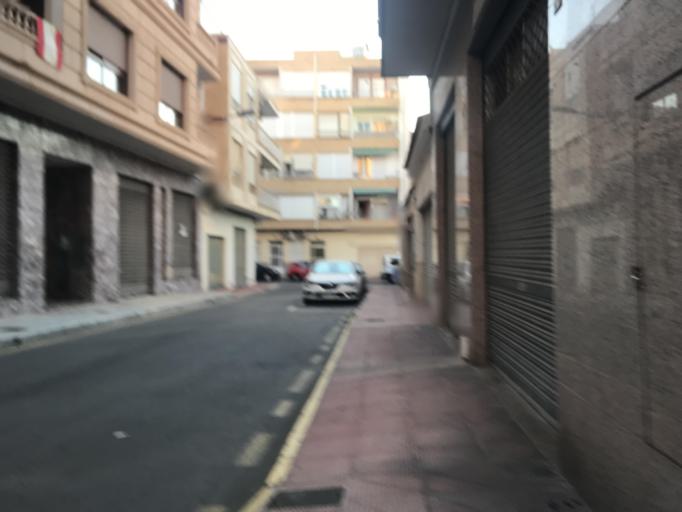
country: ES
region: Valencia
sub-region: Provincia de Alicante
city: Torrevieja
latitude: 37.9797
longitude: -0.6826
